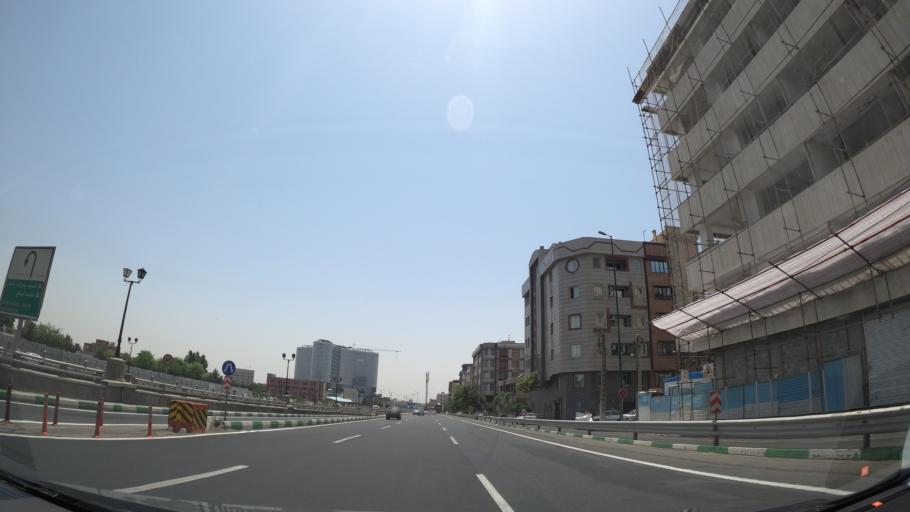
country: IR
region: Tehran
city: Tehran
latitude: 35.7137
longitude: 51.3777
